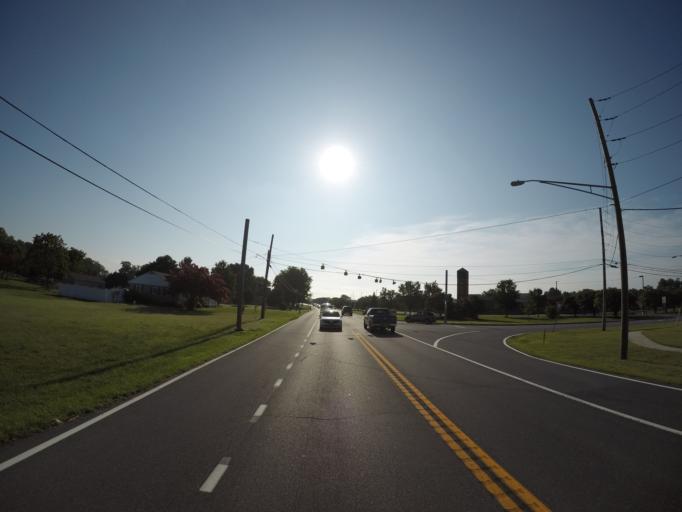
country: US
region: Delaware
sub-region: Sussex County
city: Georgetown
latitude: 38.6978
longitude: -75.4130
